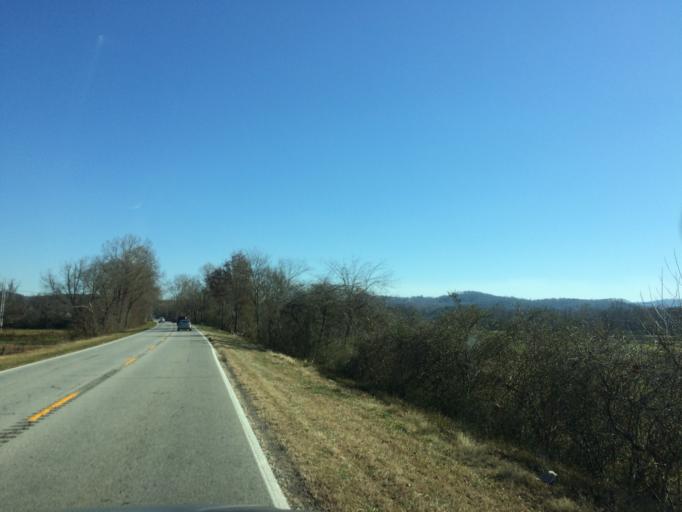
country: US
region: North Carolina
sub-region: Henderson County
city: Mills River
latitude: 35.3758
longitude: -82.5426
